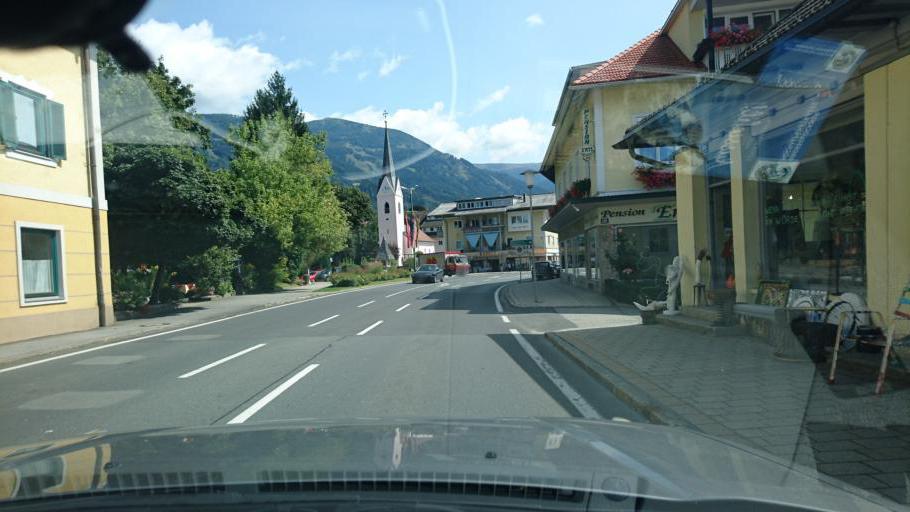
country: AT
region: Carinthia
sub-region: Politischer Bezirk Spittal an der Drau
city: Seeboden
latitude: 46.8192
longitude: 13.5205
